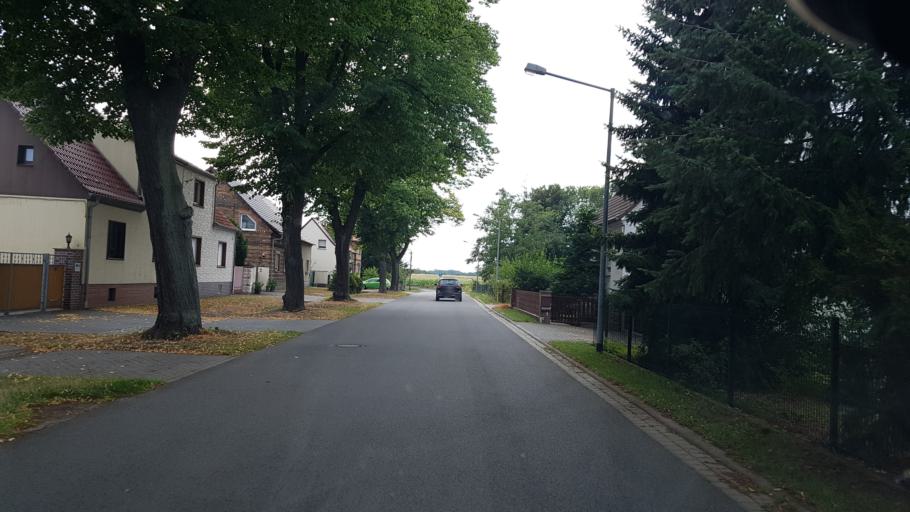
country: DE
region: Brandenburg
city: Lauchhammer
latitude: 51.5116
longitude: 13.6954
